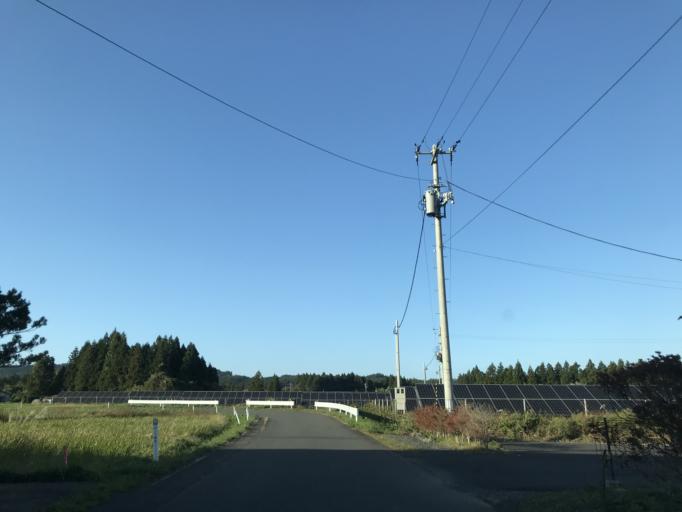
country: JP
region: Iwate
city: Ichinoseki
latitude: 38.9399
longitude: 141.0535
